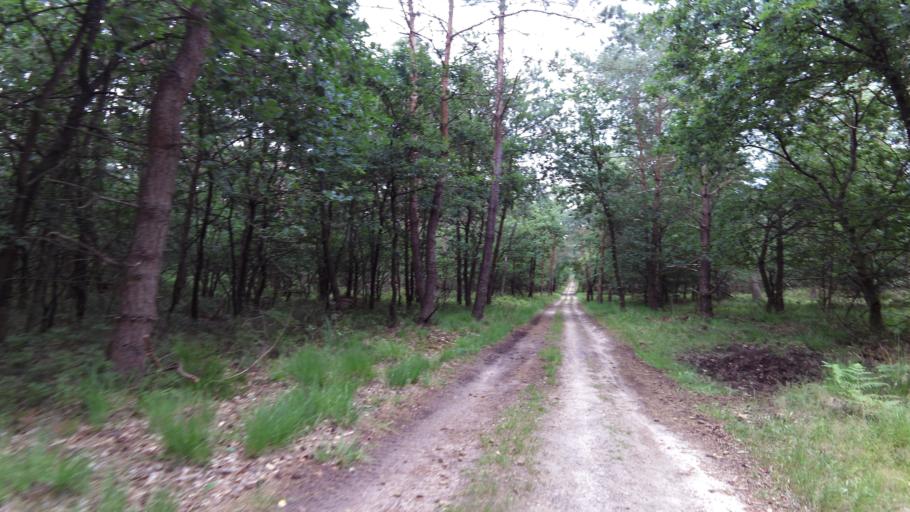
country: NL
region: Gelderland
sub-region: Gemeente Apeldoorn
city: Apeldoorn
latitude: 52.2092
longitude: 5.8736
